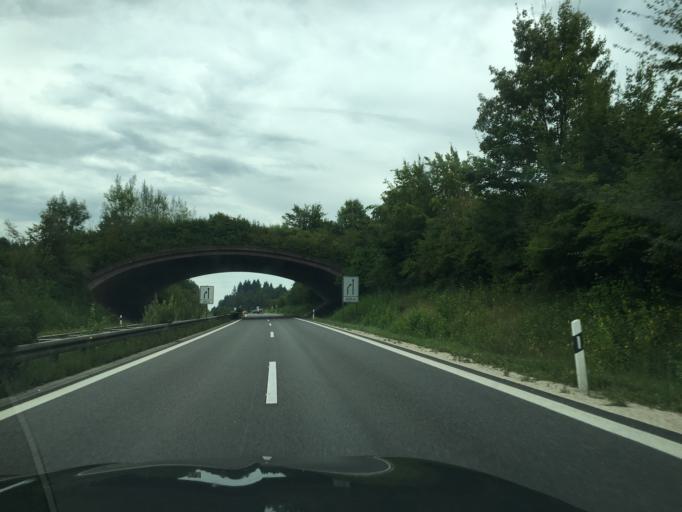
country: DE
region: Baden-Wuerttemberg
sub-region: Freiburg Region
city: Radolfzell am Bodensee
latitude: 47.7393
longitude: 9.0183
